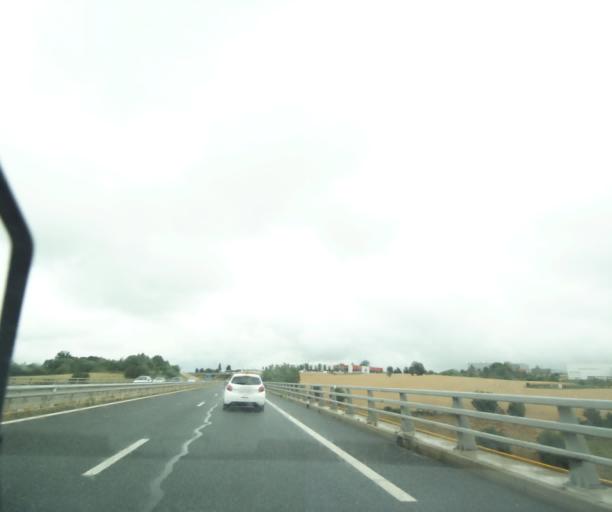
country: FR
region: Midi-Pyrenees
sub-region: Departement de l'Aveyron
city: Luc-la-Primaube
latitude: 44.3230
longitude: 2.5537
